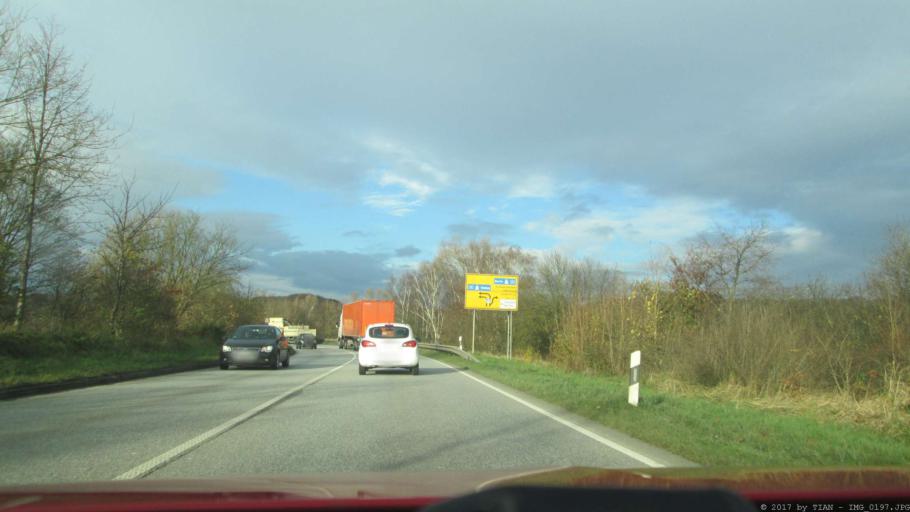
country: DE
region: Schleswig-Holstein
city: Escheburg
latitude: 53.4611
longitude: 10.3242
